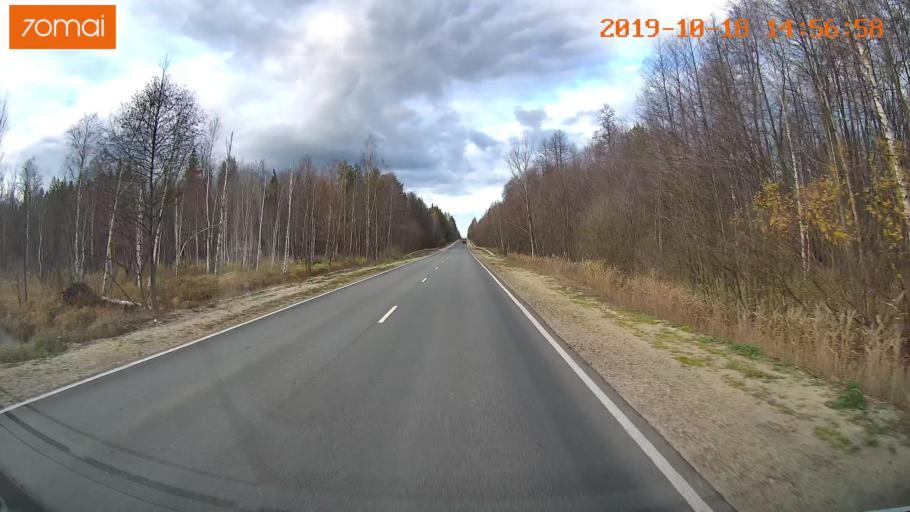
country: RU
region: Vladimir
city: Kurlovo
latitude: 55.4726
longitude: 40.5845
